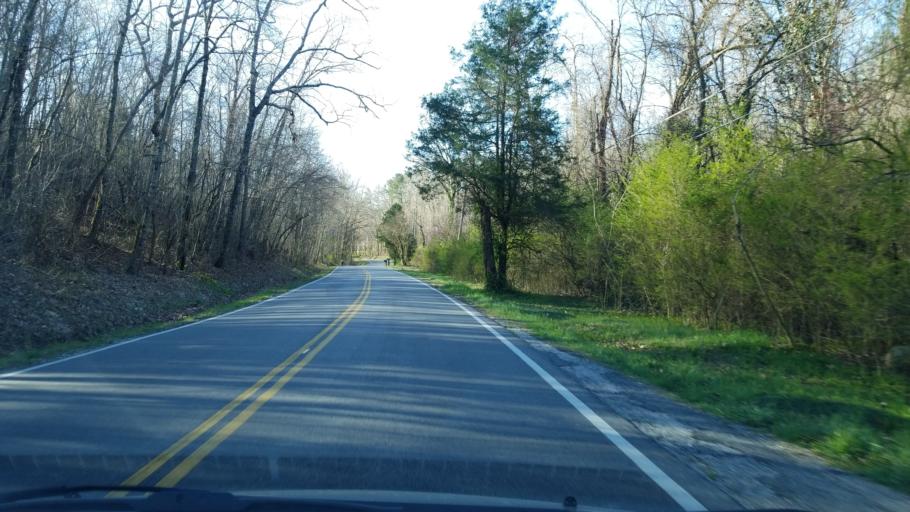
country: US
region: Tennessee
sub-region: Hamilton County
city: East Brainerd
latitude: 35.0204
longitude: -85.1137
